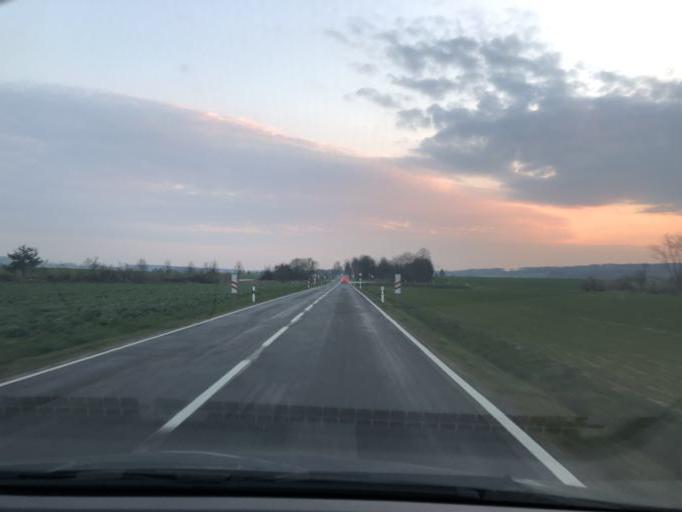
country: DE
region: Saxony
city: Haselbachtal
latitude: 51.2387
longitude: 14.0574
